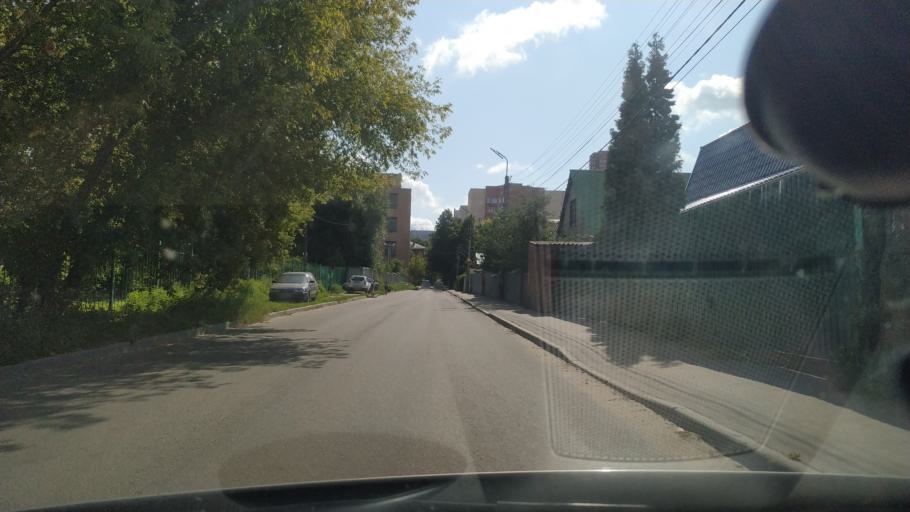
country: RU
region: Rjazan
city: Ryazan'
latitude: 54.6161
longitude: 39.7090
